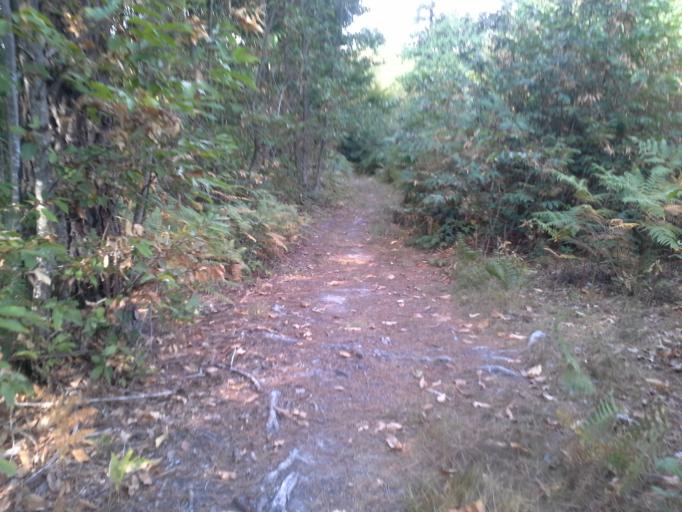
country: FR
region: Centre
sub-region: Departement du Loir-et-Cher
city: Villiers-sur-Loir
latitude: 47.8159
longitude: 1.0036
